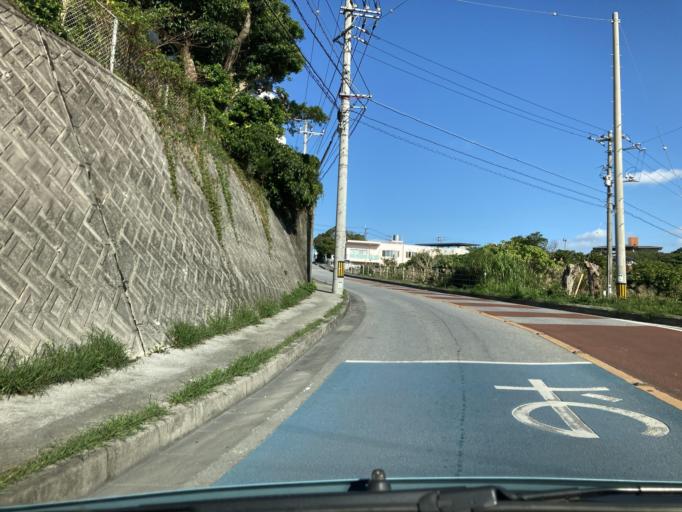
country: JP
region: Okinawa
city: Ginowan
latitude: 26.2159
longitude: 127.7418
